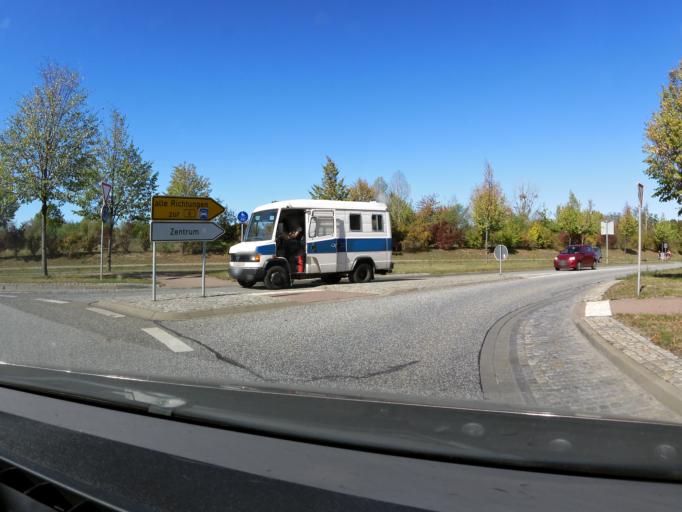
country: DE
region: Saxony-Anhalt
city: Quedlinburg
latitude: 51.7722
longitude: 11.1406
